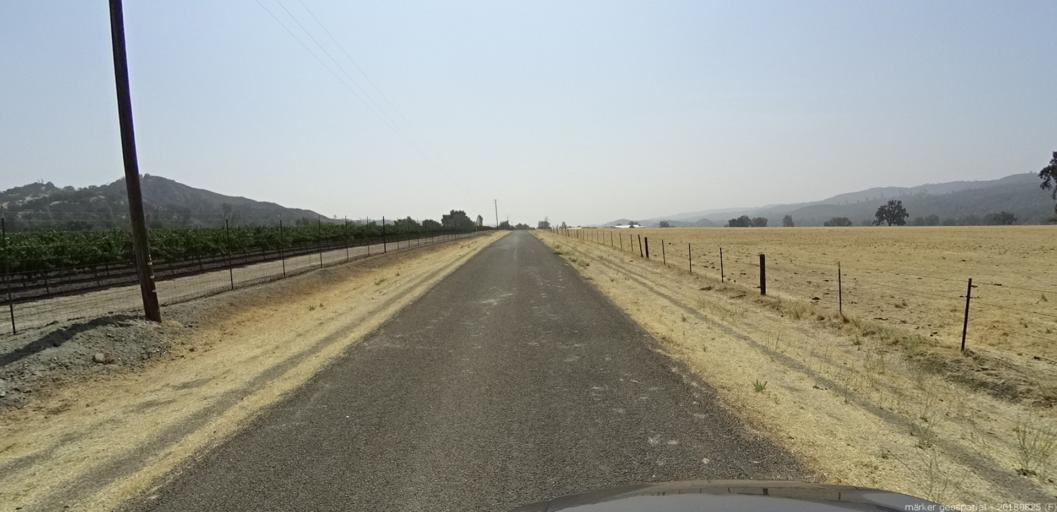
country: US
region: California
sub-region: Fresno County
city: Coalinga
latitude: 35.9486
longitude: -120.5287
